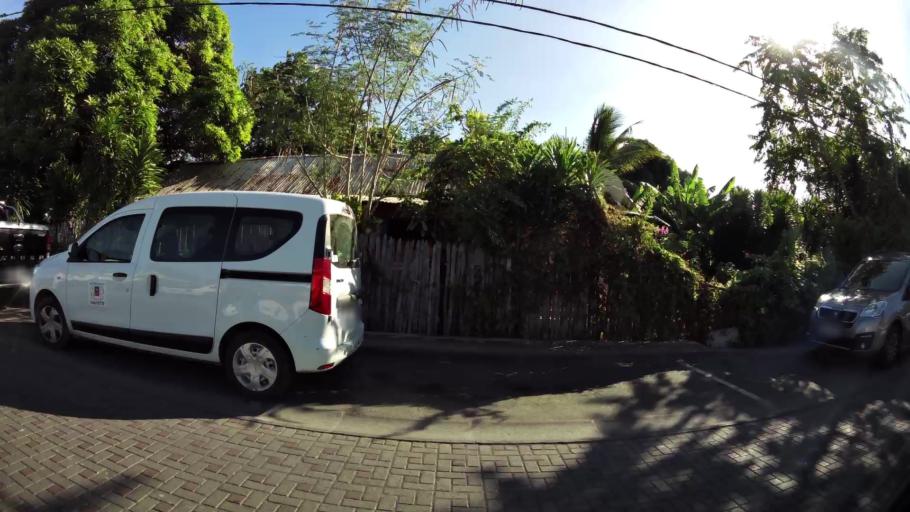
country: YT
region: Pamandzi
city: Pamandzi
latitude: -12.7984
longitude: 45.2745
